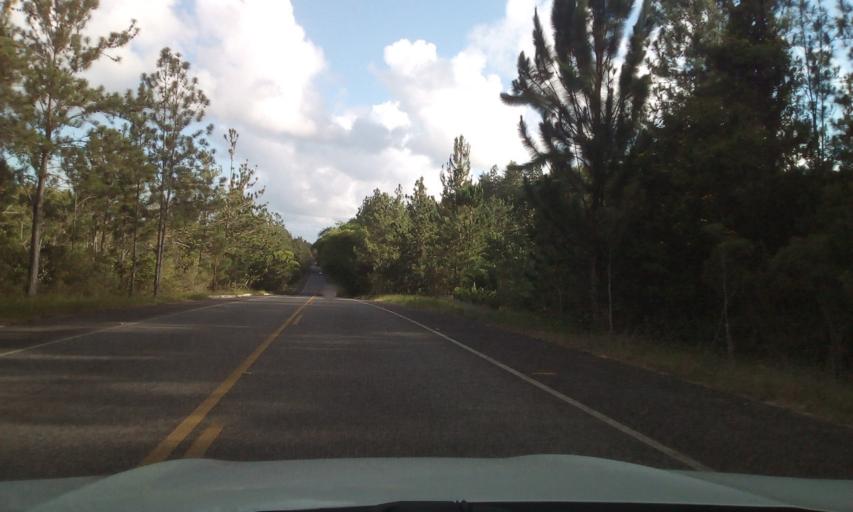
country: BR
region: Bahia
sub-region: Entre Rios
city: Entre Rios
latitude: -12.1201
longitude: -37.7883
